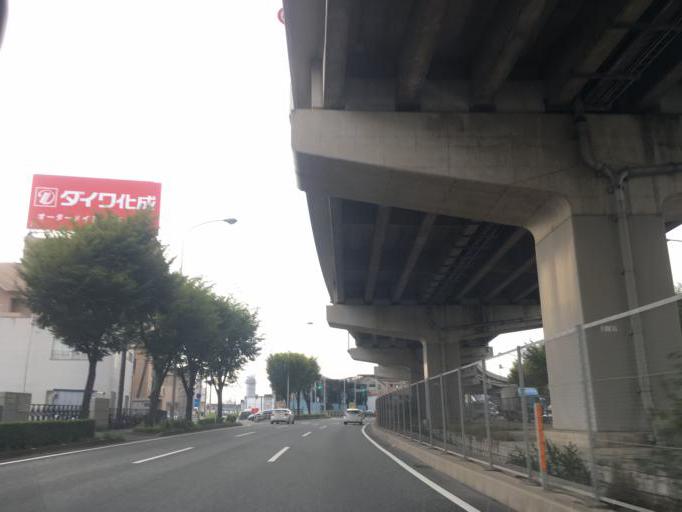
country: JP
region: Fukuoka
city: Fukuoka-shi
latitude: 33.5902
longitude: 130.4381
